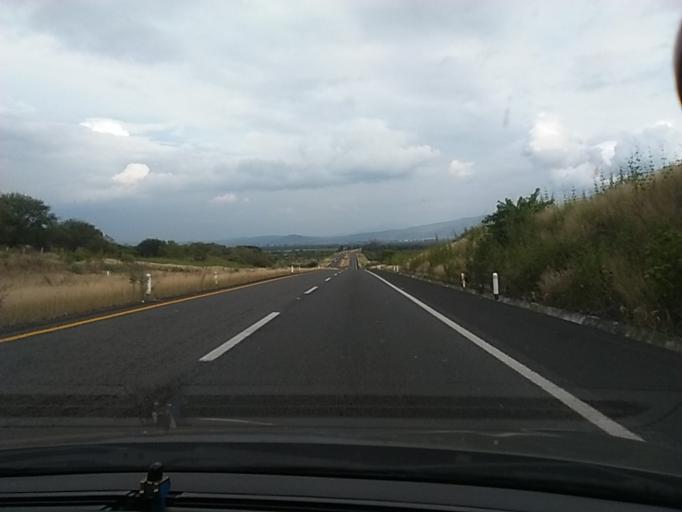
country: MX
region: Michoacan
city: Ixtlan
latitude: 20.1845
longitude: -102.2971
